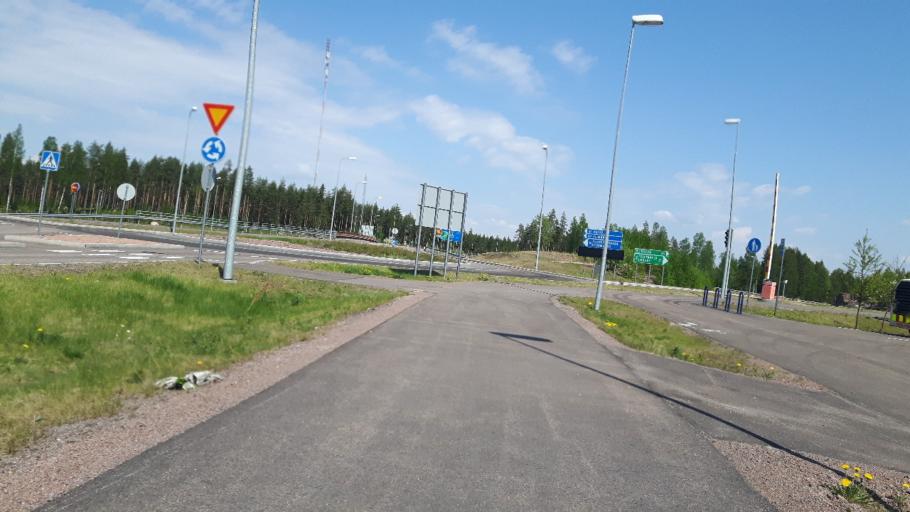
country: FI
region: Uusimaa
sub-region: Loviisa
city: Ruotsinpyhtaeae
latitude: 60.4909
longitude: 26.4187
